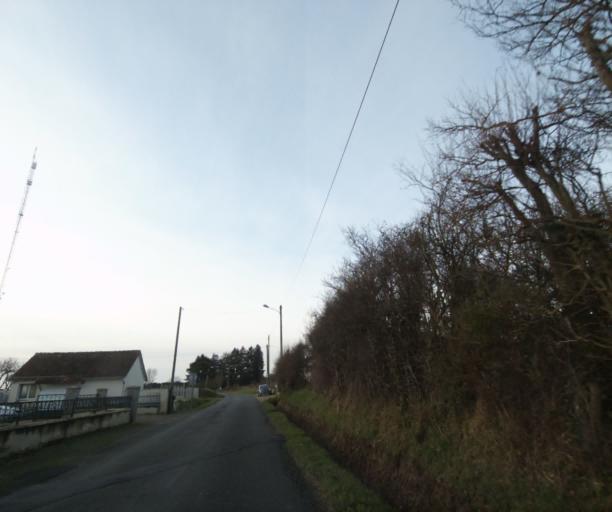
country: FR
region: Pays de la Loire
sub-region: Departement de la Sarthe
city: Rouillon
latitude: 48.0042
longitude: 0.1636
